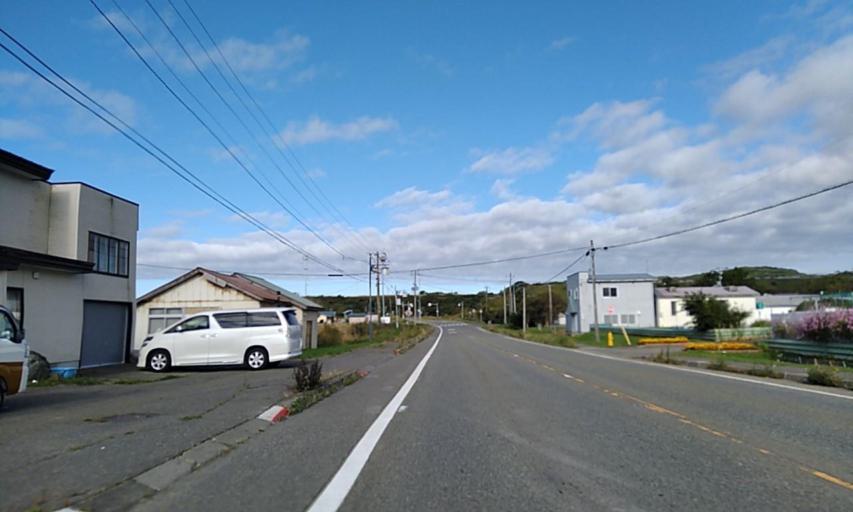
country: JP
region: Hokkaido
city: Shizunai-furukawacho
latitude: 42.2459
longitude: 142.5775
